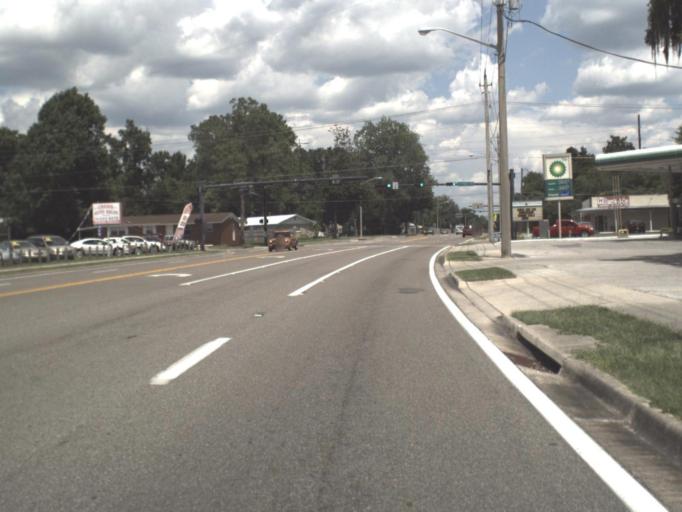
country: US
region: Florida
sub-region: Columbia County
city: Watertown
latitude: 30.1833
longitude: -82.6105
